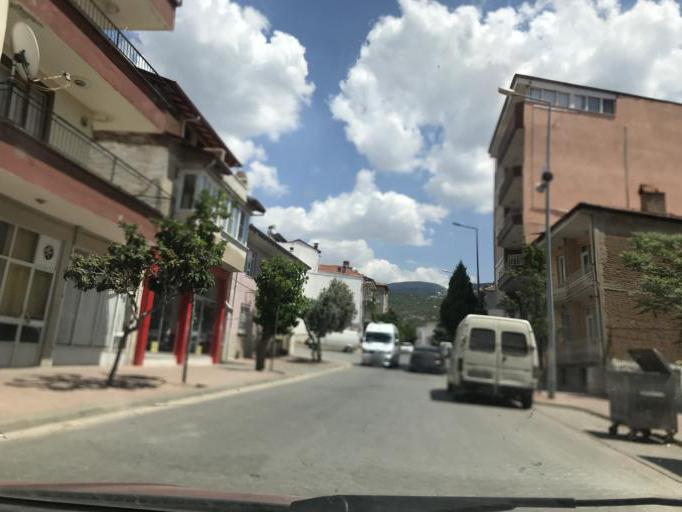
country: TR
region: Denizli
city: Tavas
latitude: 37.5749
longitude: 29.0665
